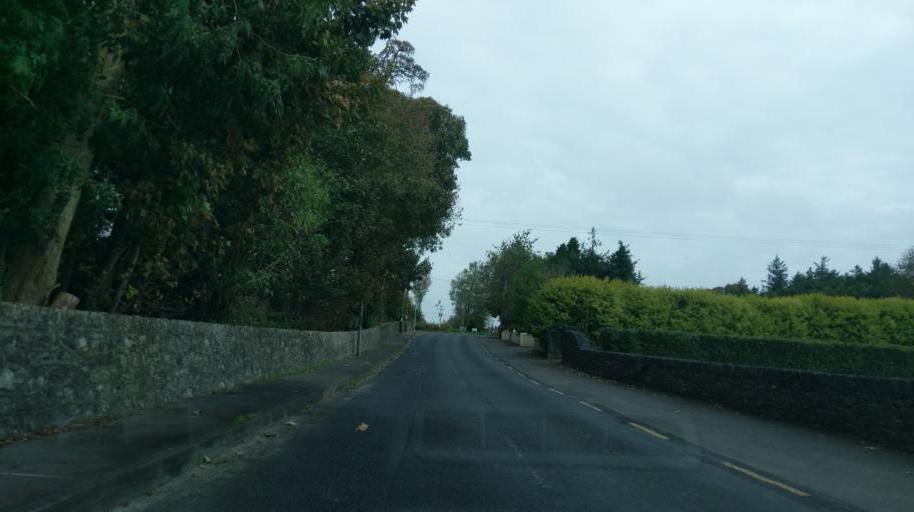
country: IE
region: Connaught
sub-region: County Galway
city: Athenry
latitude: 53.3730
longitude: -8.7012
